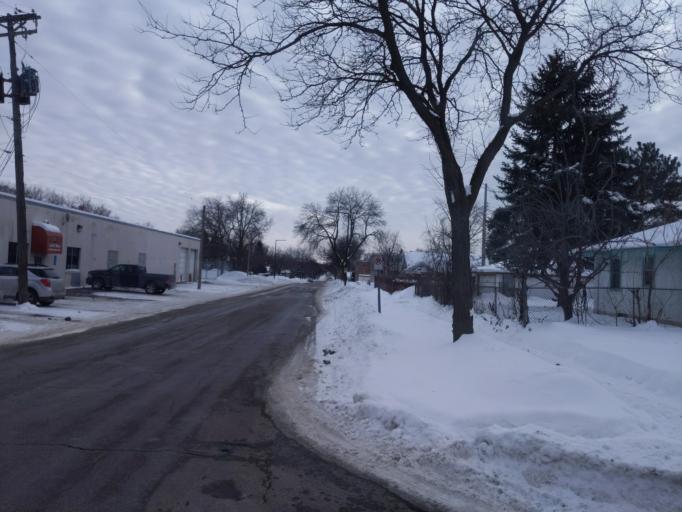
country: US
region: Minnesota
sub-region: Ramsey County
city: Falcon Heights
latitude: 44.9630
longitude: -93.1416
